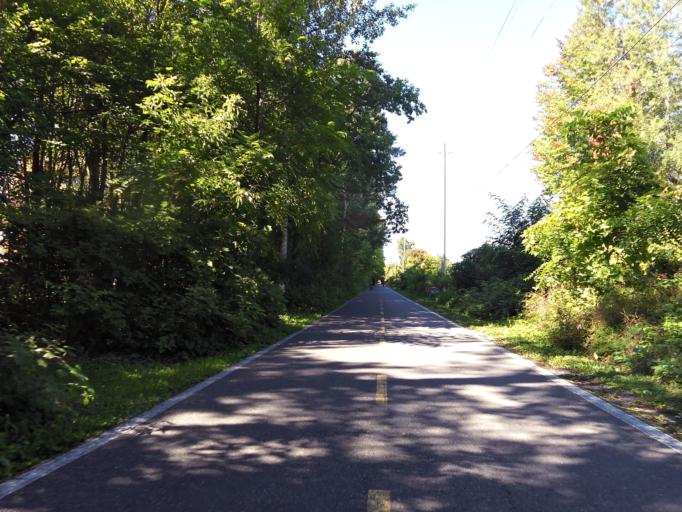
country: CA
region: Ontario
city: Bourget
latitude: 45.2638
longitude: -75.3554
